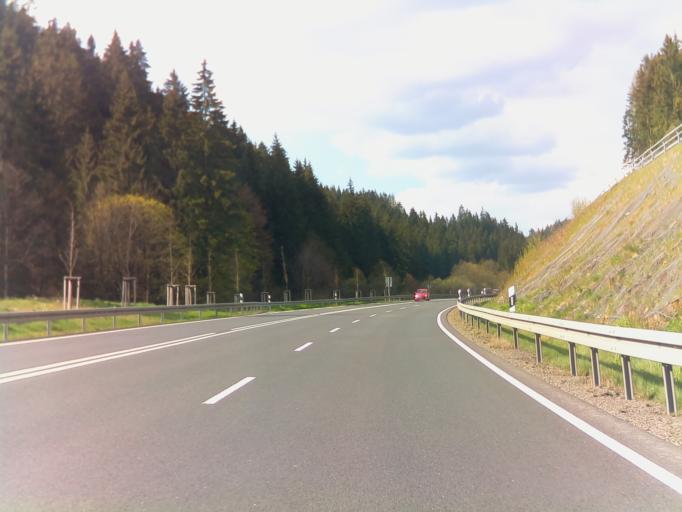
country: DE
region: Bavaria
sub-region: Upper Franconia
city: Teuschnitz
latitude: 50.4041
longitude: 11.3522
